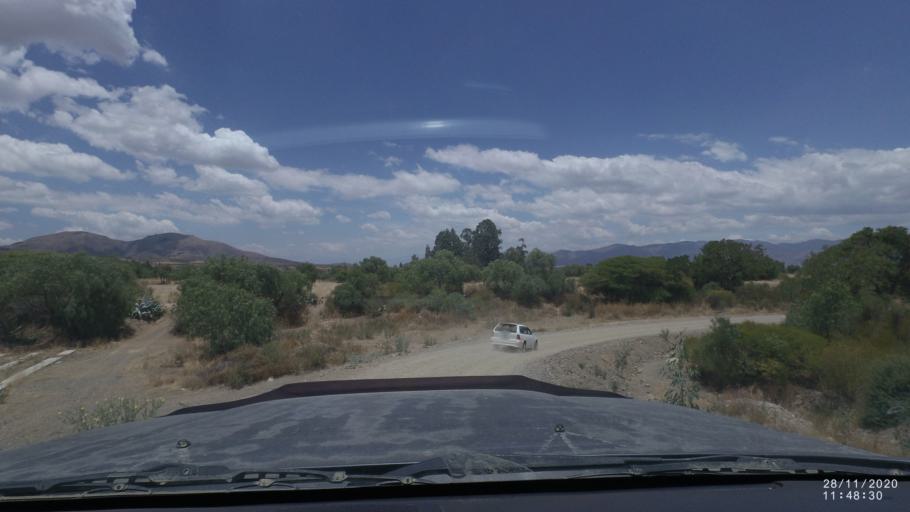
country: BO
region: Cochabamba
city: Tarata
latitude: -17.6385
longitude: -66.0325
